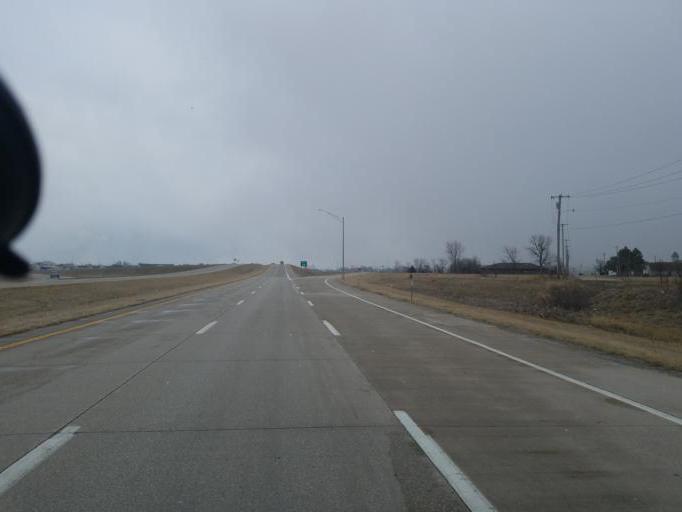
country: US
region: Missouri
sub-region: Randolph County
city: Moberly
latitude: 39.4485
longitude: -92.4277
